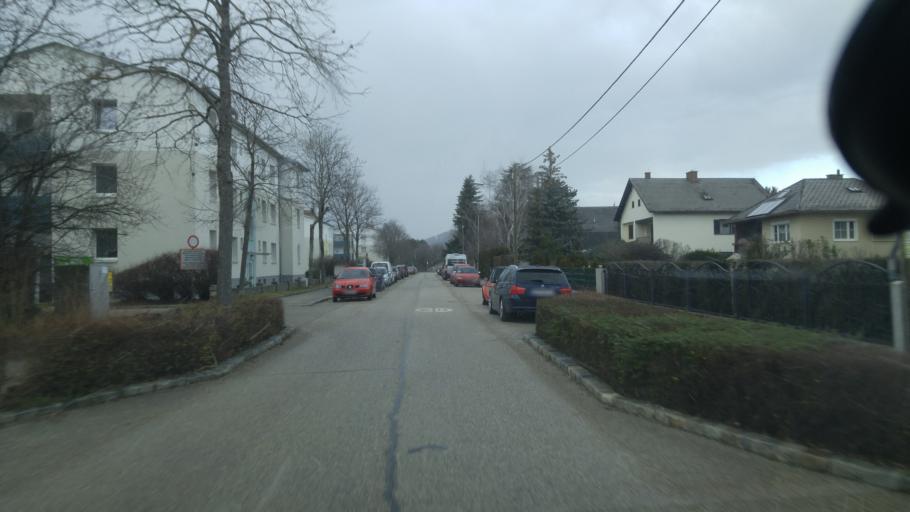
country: AT
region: Lower Austria
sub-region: Politischer Bezirk Baden
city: Baden
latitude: 47.9960
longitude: 16.2238
